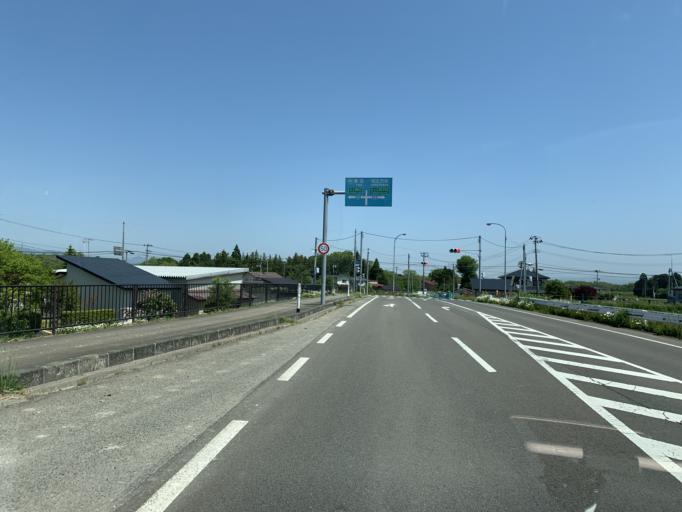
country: JP
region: Iwate
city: Kitakami
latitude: 39.2823
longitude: 141.0510
